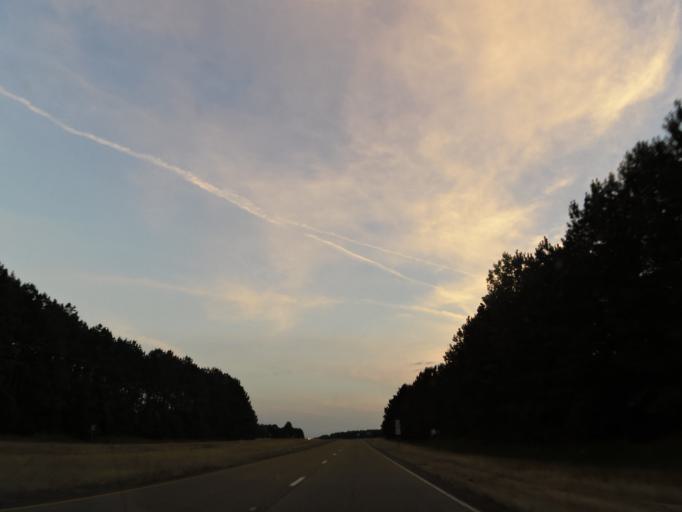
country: US
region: Mississippi
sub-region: Kemper County
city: De Kalb
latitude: 32.6899
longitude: -88.4880
